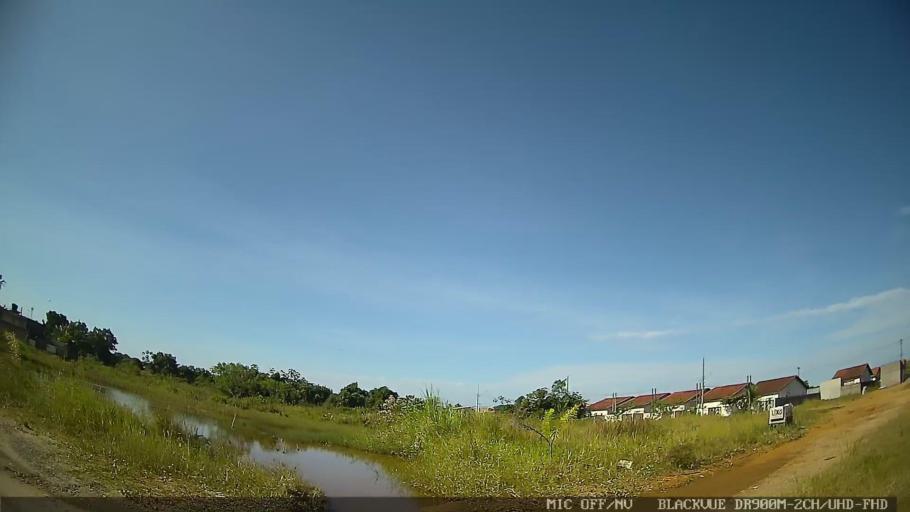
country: BR
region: Sao Paulo
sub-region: Itanhaem
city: Itanhaem
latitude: -24.2190
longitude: -46.8699
